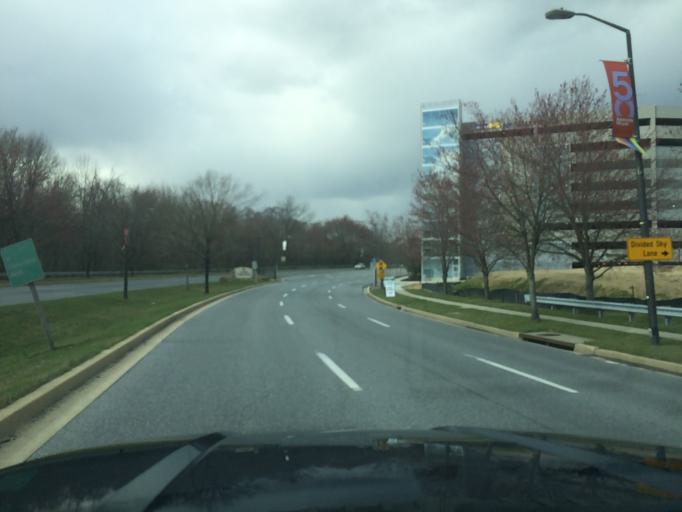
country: US
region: Maryland
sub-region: Howard County
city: Riverside
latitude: 39.2092
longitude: -76.8674
